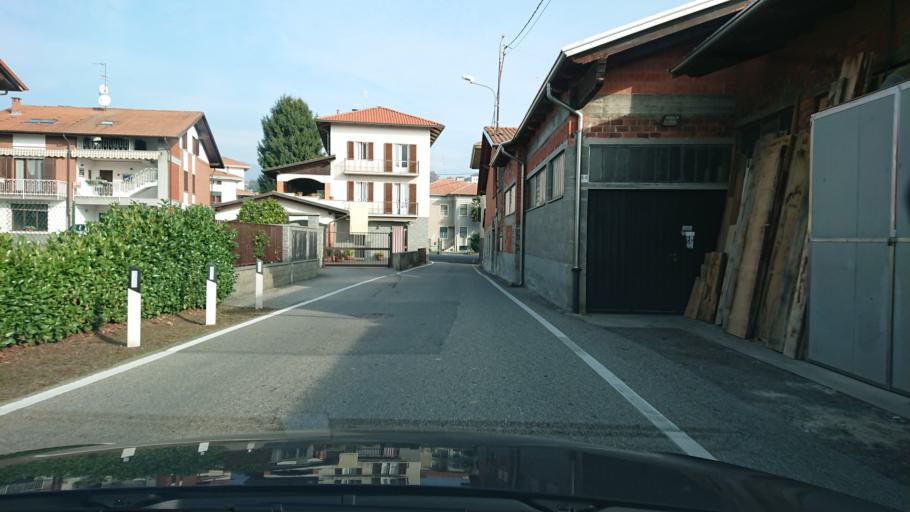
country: IT
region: Piedmont
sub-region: Provincia di Biella
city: Valdengo
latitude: 45.5682
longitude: 8.1319
